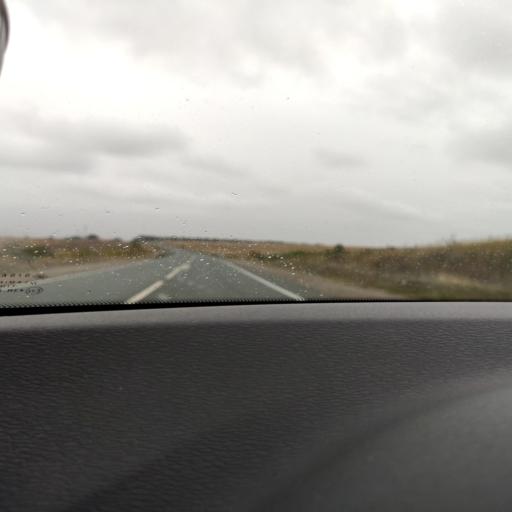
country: RU
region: Samara
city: Mirnyy
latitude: 53.5939
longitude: 50.2783
